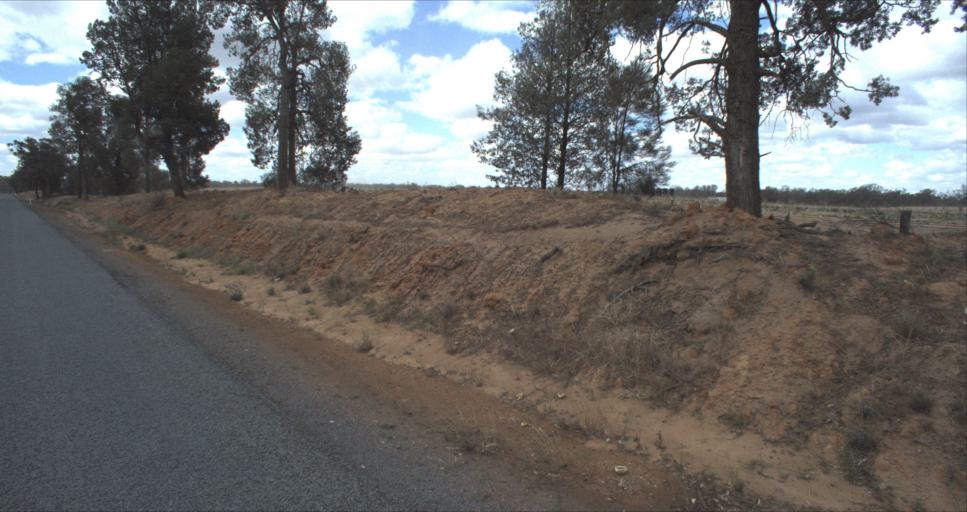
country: AU
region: New South Wales
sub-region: Leeton
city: Leeton
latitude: -34.6523
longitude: 146.3510
